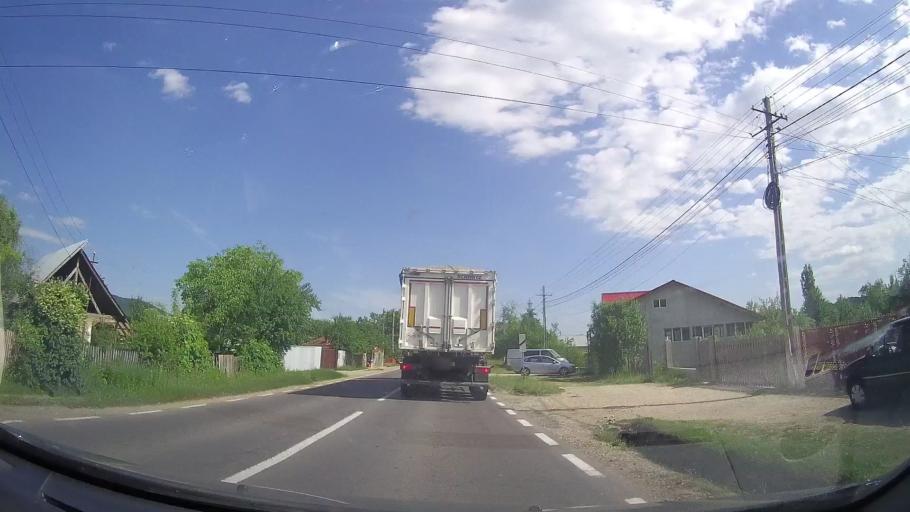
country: RO
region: Prahova
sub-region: Comuna Maneciu-Ungureni
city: Gheaba
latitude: 45.3033
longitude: 25.9960
